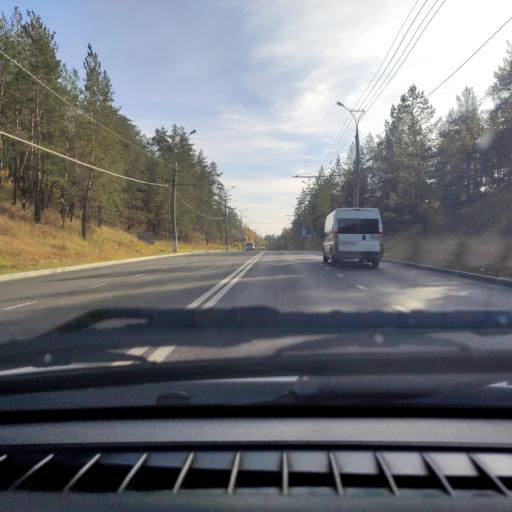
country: RU
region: Samara
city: Zhigulevsk
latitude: 53.4944
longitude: 49.4629
